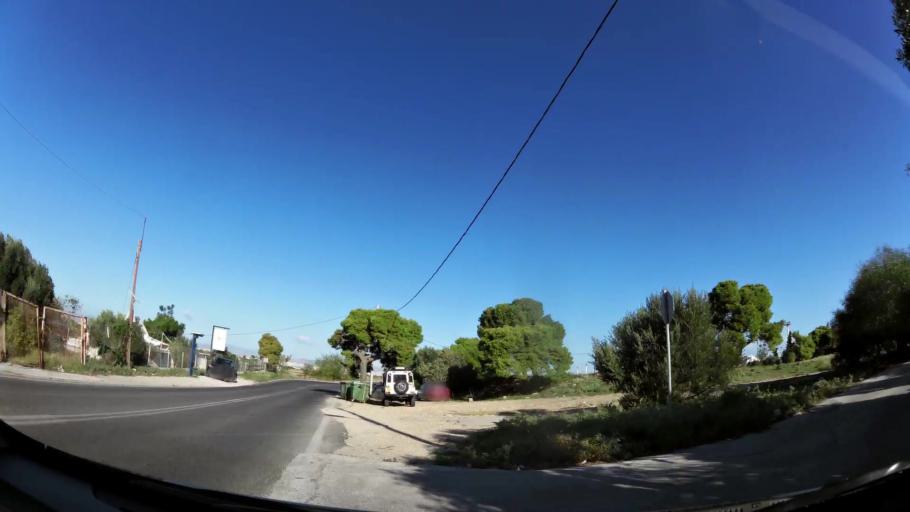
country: GR
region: Attica
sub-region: Nomarchia Athinas
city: Elliniko
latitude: 37.8769
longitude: 23.7434
